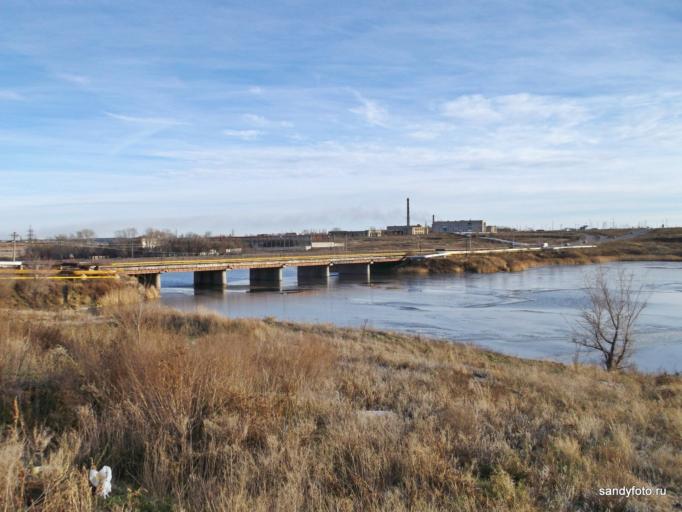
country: RU
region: Chelyabinsk
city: Troitsk
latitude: 54.0763
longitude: 61.5535
